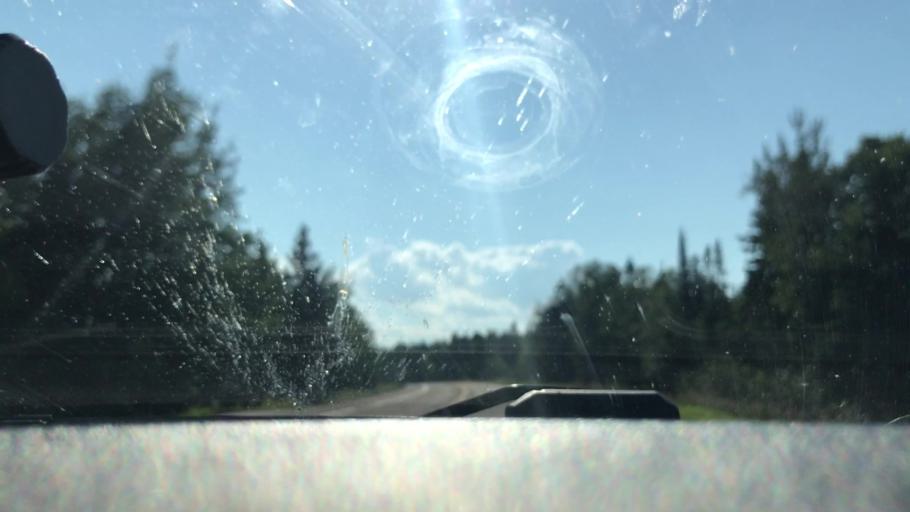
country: US
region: Minnesota
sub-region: Cook County
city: Grand Marais
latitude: 47.8290
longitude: -89.9946
